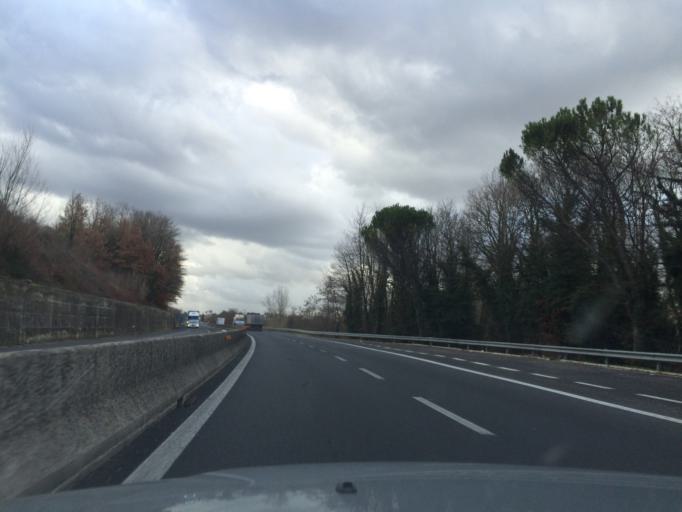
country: IT
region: Umbria
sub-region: Provincia di Terni
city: Acquasparta
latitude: 42.6514
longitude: 12.5365
